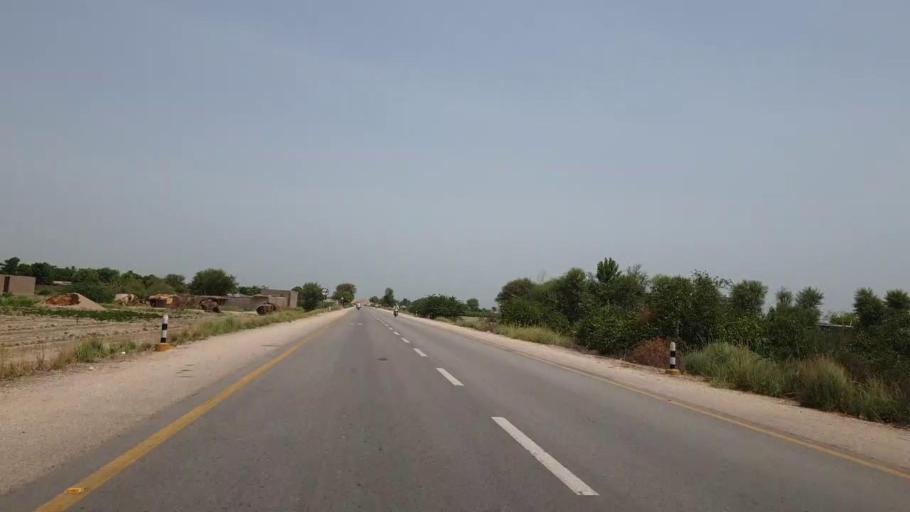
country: PK
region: Sindh
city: Shahpur Chakar
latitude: 26.1593
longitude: 68.6316
